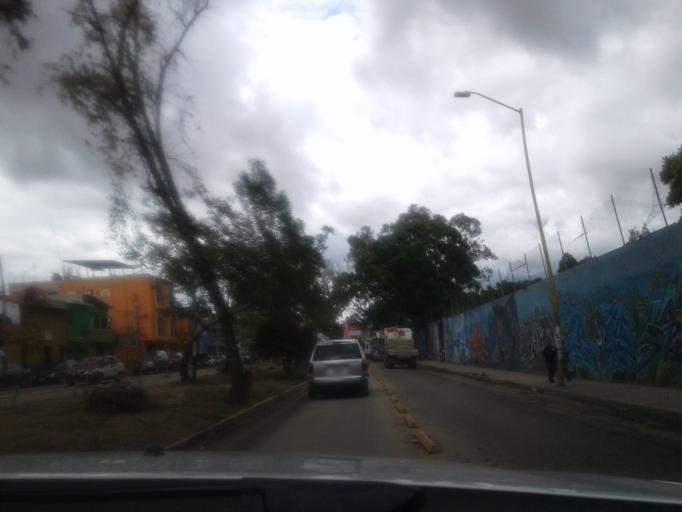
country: MX
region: Oaxaca
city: Oaxaca de Juarez
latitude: 17.0535
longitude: -96.7295
